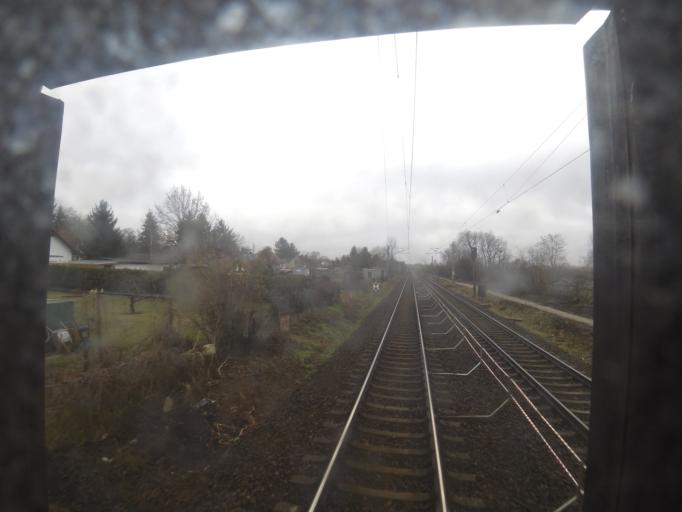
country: DE
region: Brandenburg
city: Rangsdorf
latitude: 52.2838
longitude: 13.4344
